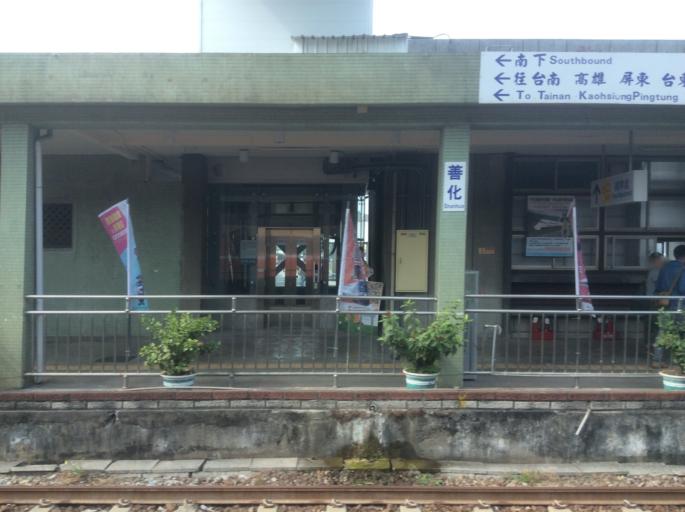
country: TW
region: Taiwan
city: Yujing
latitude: 23.1332
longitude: 120.3066
